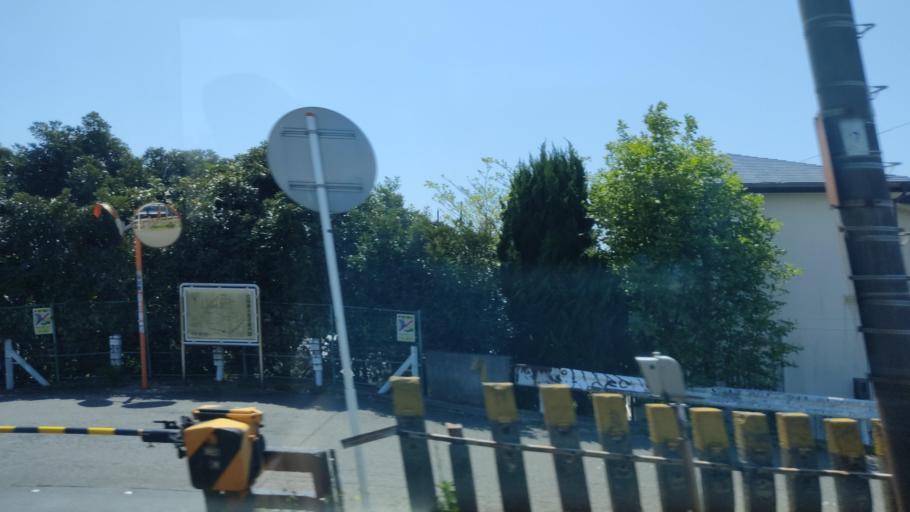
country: JP
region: Kanagawa
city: Chigasaki
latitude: 35.3289
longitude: 139.3842
